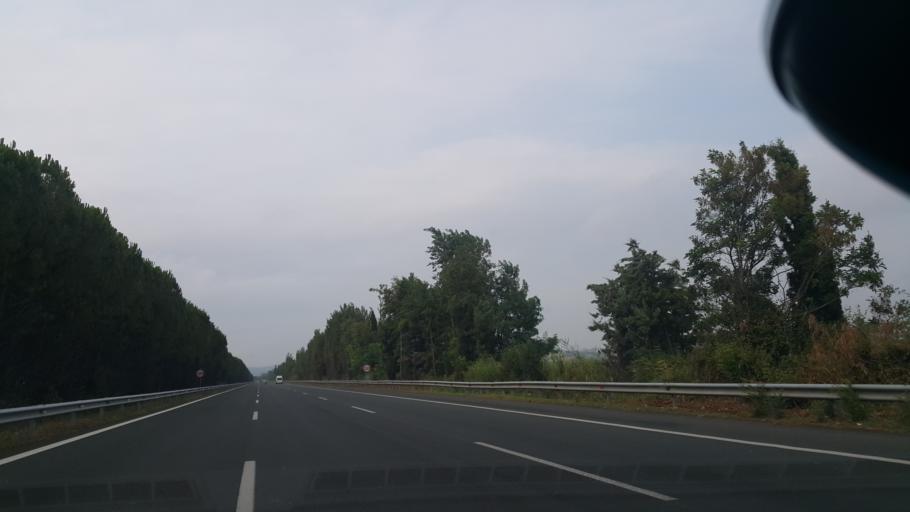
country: GR
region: Central Macedonia
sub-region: Nomos Pierias
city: Aiginio
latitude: 40.5092
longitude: 22.5688
